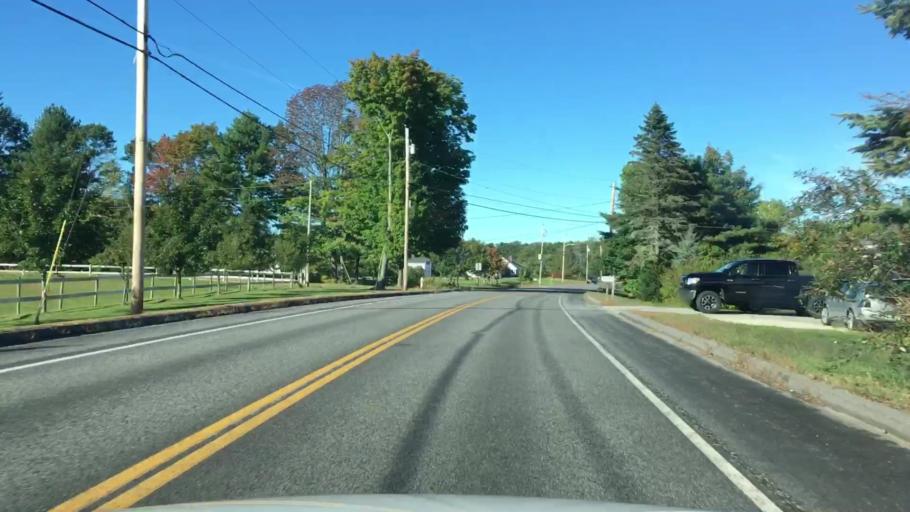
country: US
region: Maine
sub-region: Androscoggin County
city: Lisbon Falls
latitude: 44.0136
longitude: -70.0693
